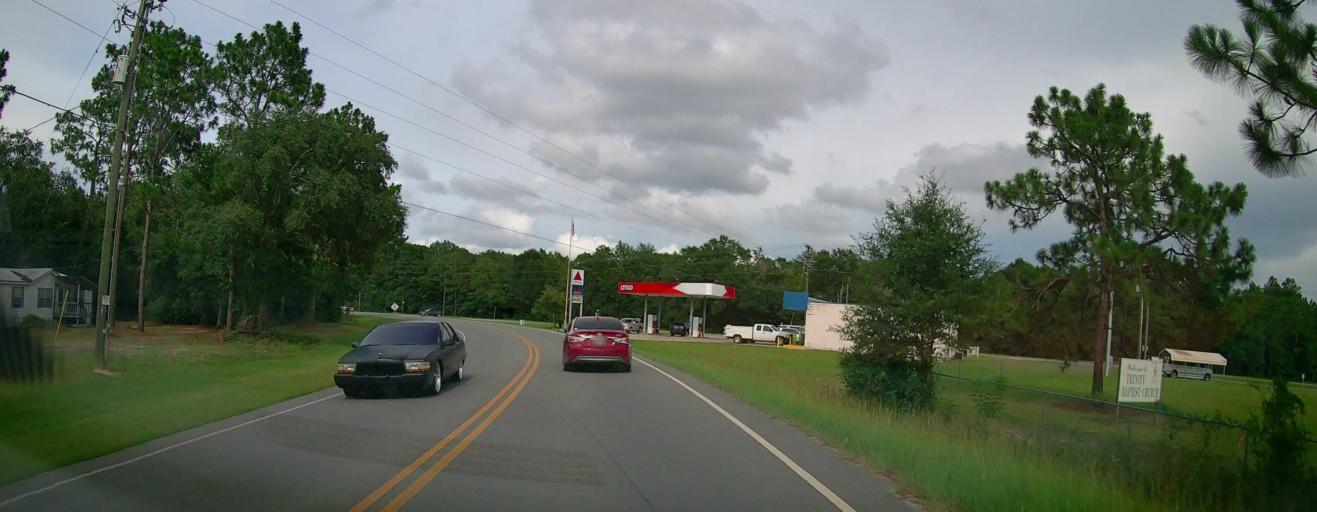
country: US
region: Georgia
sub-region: Wayne County
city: Jesup
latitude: 31.6570
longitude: -81.8925
